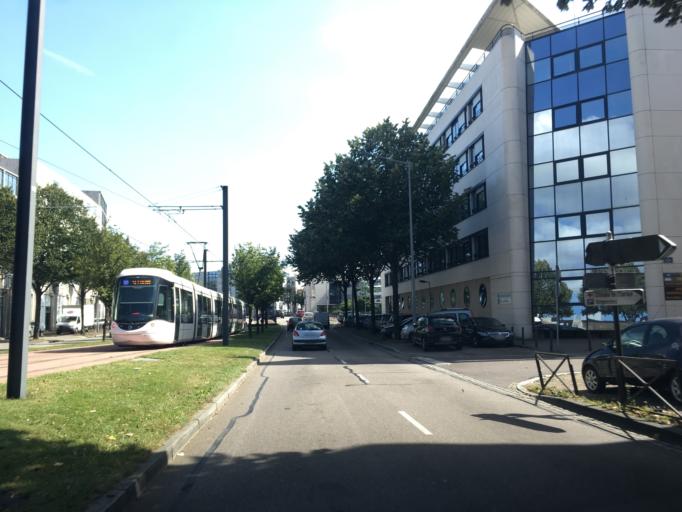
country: FR
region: Haute-Normandie
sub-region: Departement de la Seine-Maritime
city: Sotteville-les-Rouen
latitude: 49.4265
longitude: 1.0853
